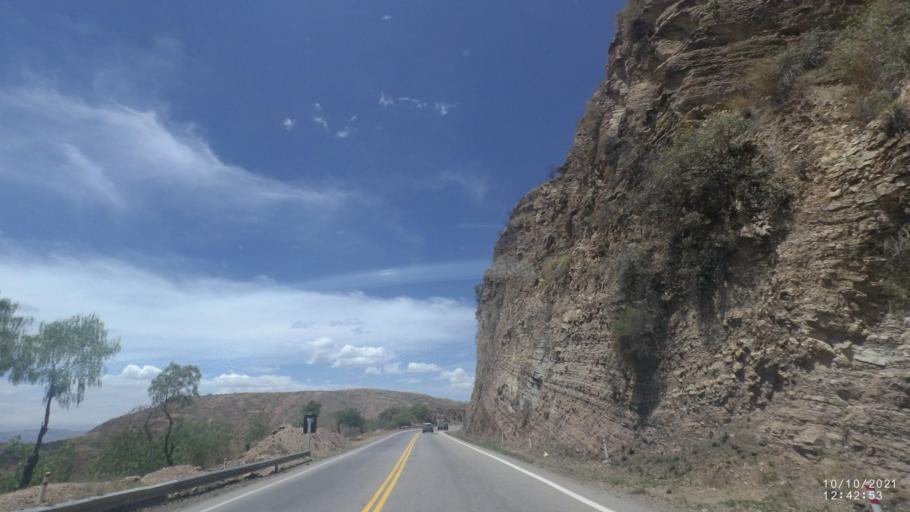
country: BO
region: Cochabamba
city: Irpa Irpa
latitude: -17.6274
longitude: -66.3912
